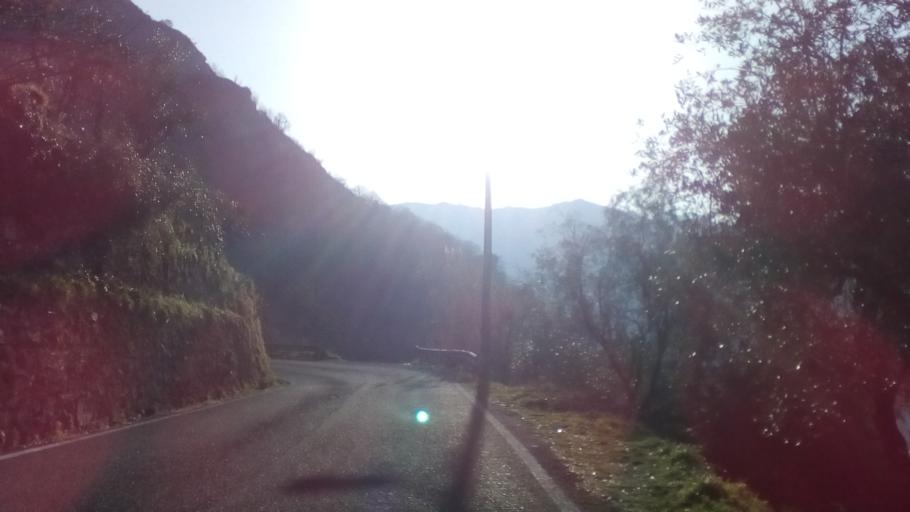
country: IT
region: Tuscany
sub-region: Provincia di Massa-Carrara
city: Montignoso
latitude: 44.0599
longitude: 10.1823
